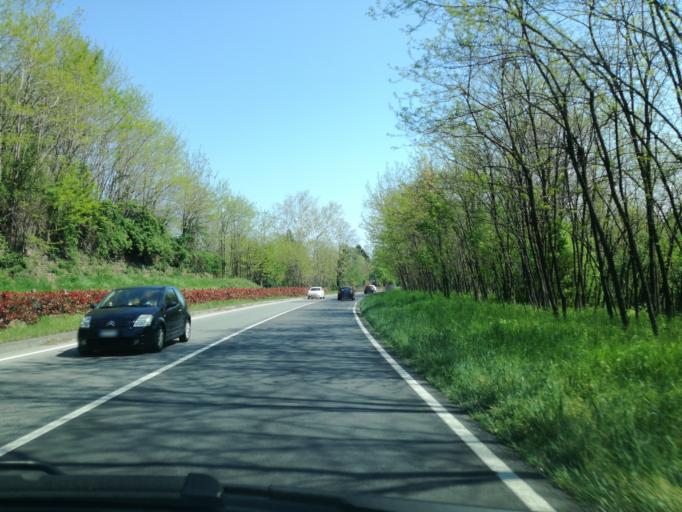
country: IT
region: Lombardy
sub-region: Provincia di Bergamo
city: Terno d'Isola
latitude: 45.6895
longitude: 9.5261
